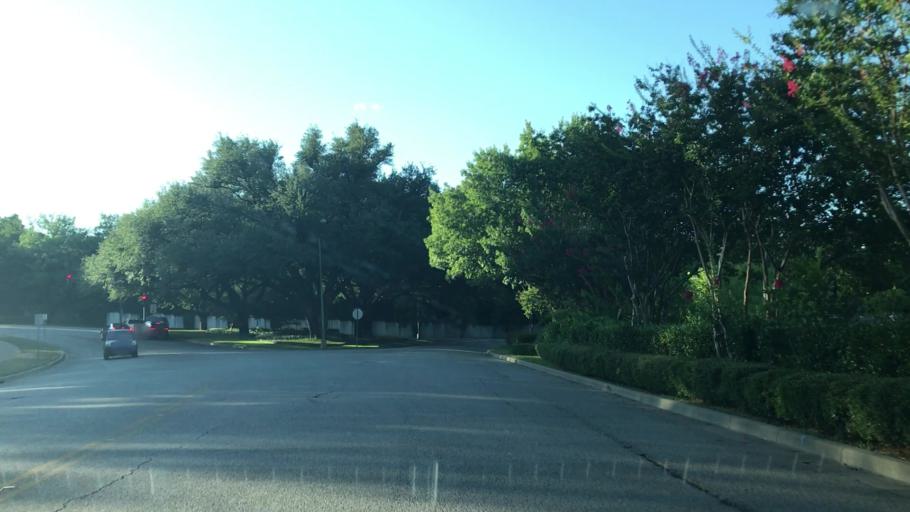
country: US
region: Texas
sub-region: Dallas County
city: Highland Park
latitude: 32.8223
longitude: -96.8009
